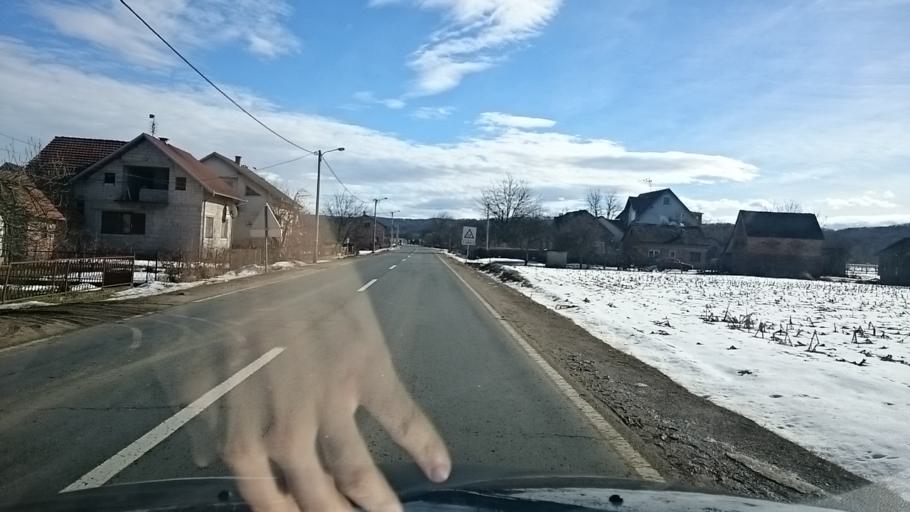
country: HR
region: Sisacko-Moslavacka
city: Novska
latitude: 45.2101
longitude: 16.9519
